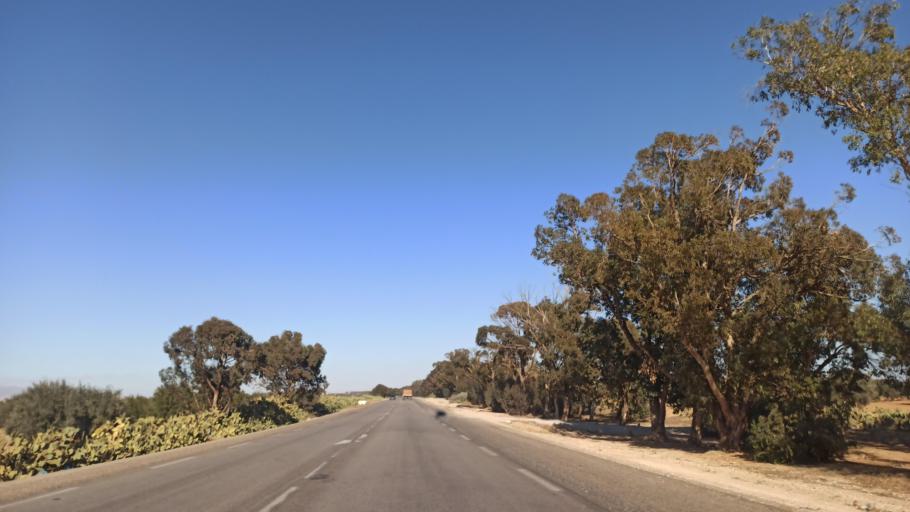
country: TN
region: Sidi Bu Zayd
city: Jilma
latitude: 35.1682
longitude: 9.3696
